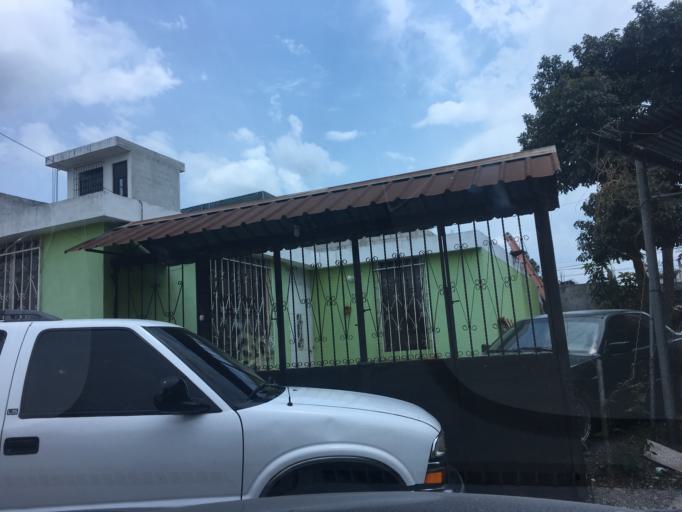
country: GT
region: Guatemala
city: Petapa
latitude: 14.5078
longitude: -90.5581
